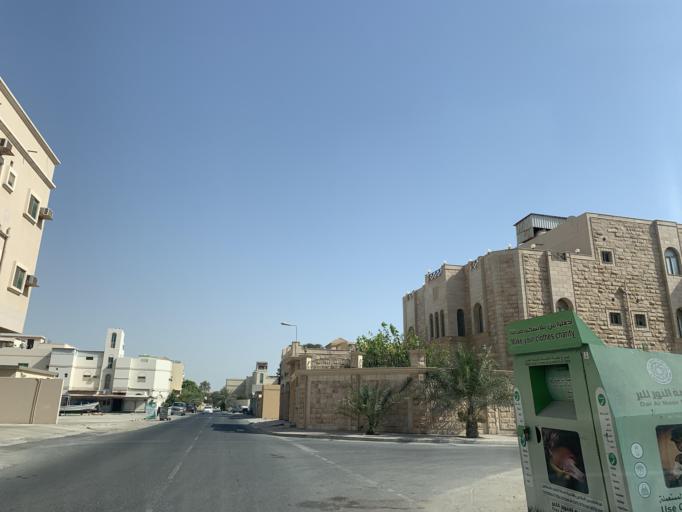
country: BH
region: Manama
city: Jidd Hafs
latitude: 26.2321
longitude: 50.4845
